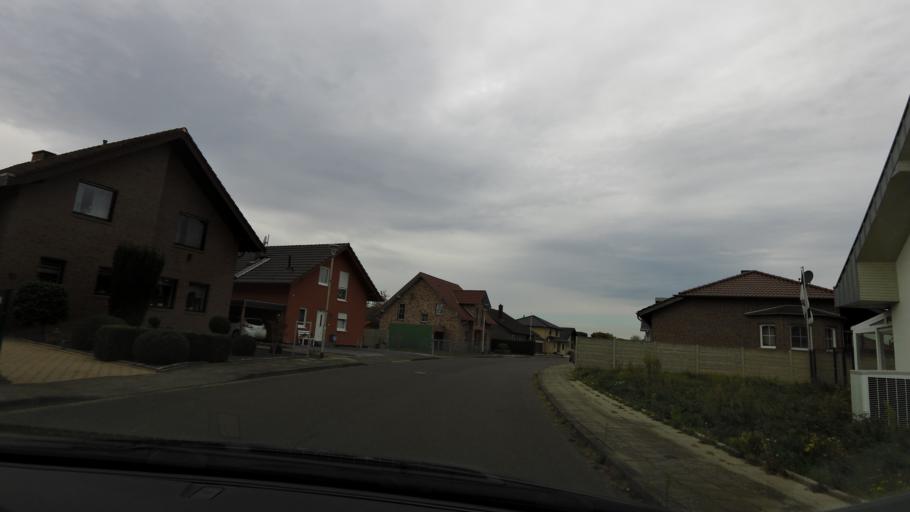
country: DE
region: North Rhine-Westphalia
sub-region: Regierungsbezirk Koln
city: Gangelt
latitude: 50.9798
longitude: 6.0376
